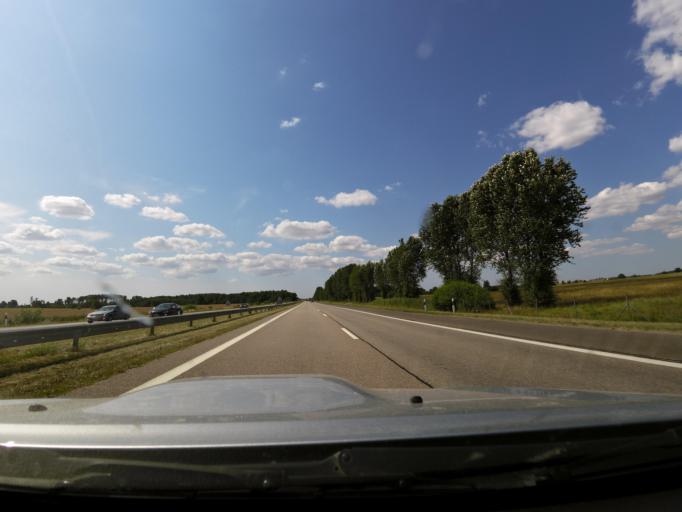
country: LT
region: Klaipedos apskritis
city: Gargzdai
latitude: 55.7084
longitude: 21.5283
